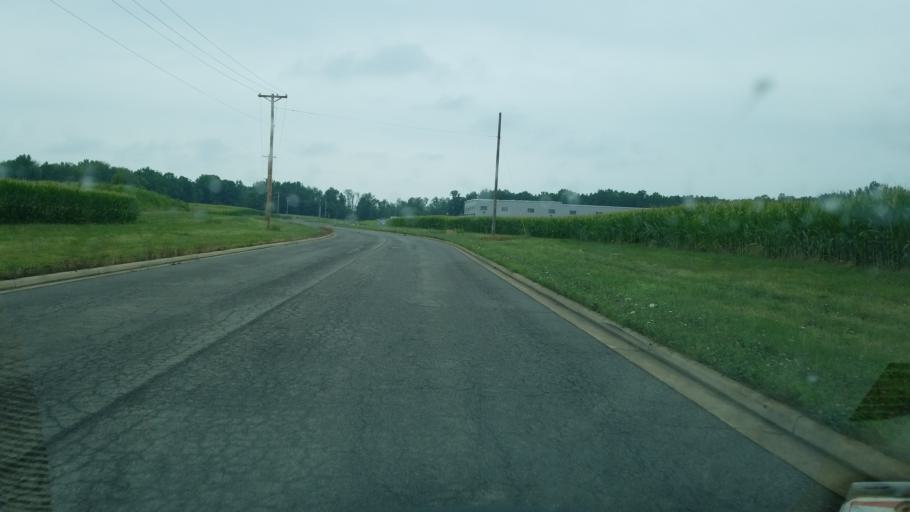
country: US
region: Ohio
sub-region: Richland County
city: Shelby
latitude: 40.8665
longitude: -82.6367
